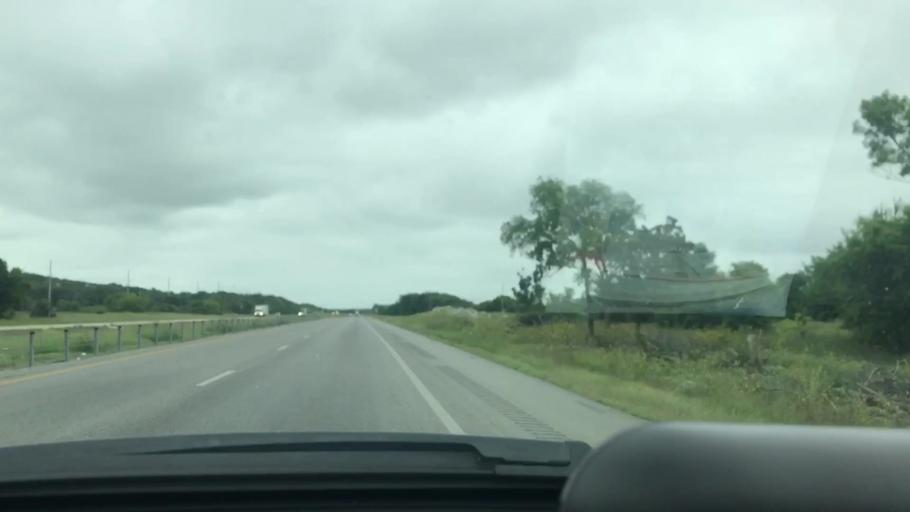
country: US
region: Oklahoma
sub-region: Coal County
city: Coalgate
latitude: 34.6344
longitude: -95.9541
